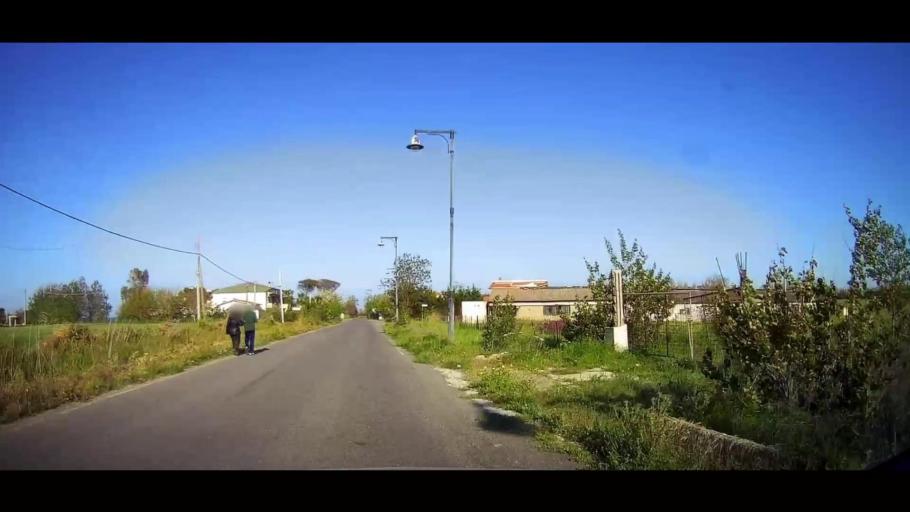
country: IT
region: Calabria
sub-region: Provincia di Crotone
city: Crotone
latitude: 39.0255
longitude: 17.1920
